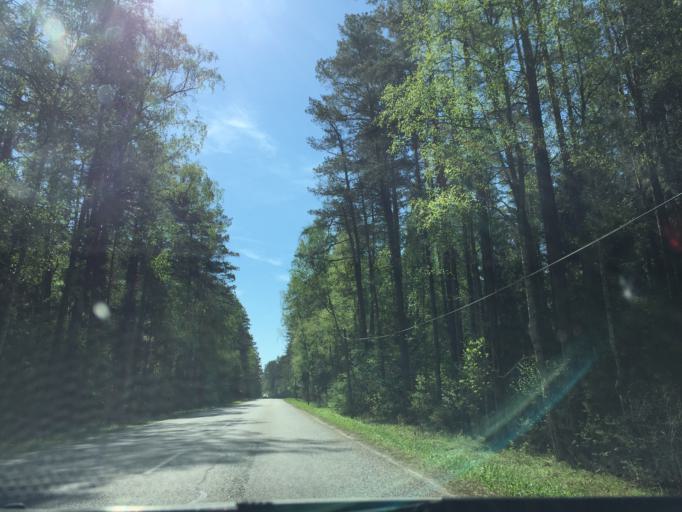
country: LV
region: Garkalne
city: Garkalne
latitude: 57.0190
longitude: 24.4396
